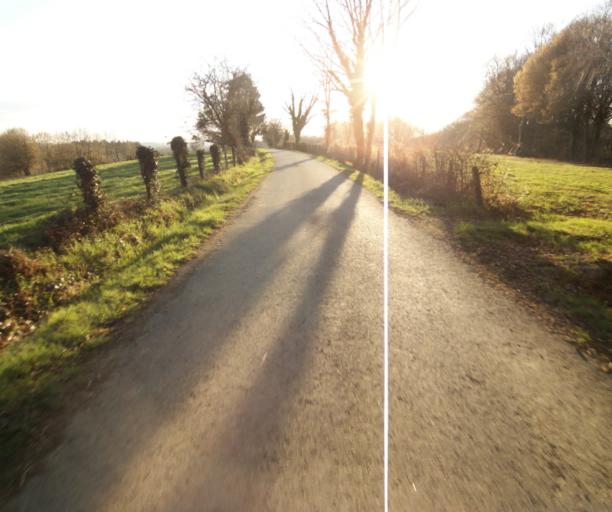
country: FR
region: Limousin
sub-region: Departement de la Correze
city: Uzerche
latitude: 45.3577
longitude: 1.5909
